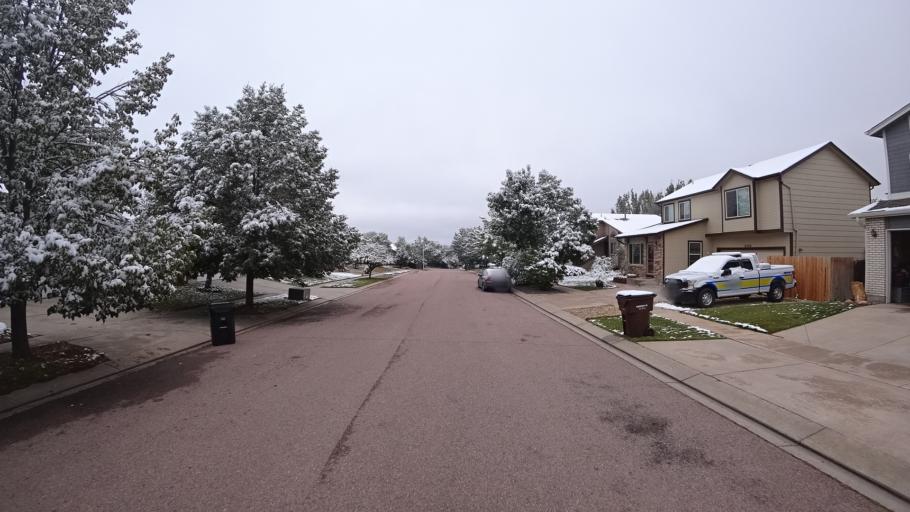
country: US
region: Colorado
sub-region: El Paso County
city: Colorado Springs
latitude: 38.9172
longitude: -104.7823
